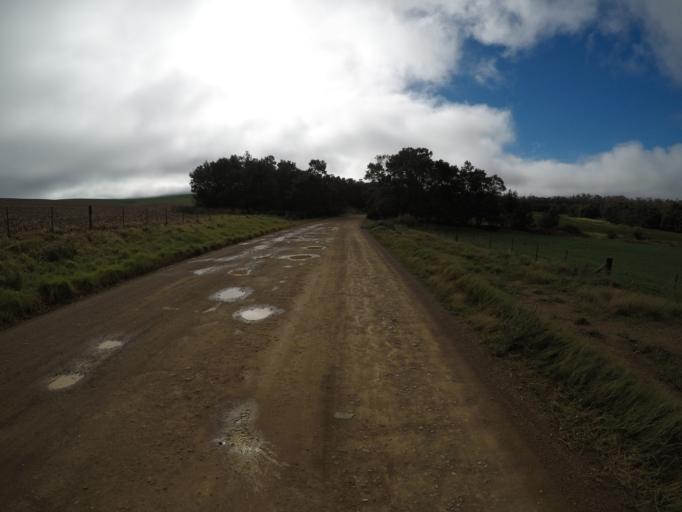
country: ZA
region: Western Cape
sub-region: Overberg District Municipality
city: Caledon
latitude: -34.1148
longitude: 19.7904
